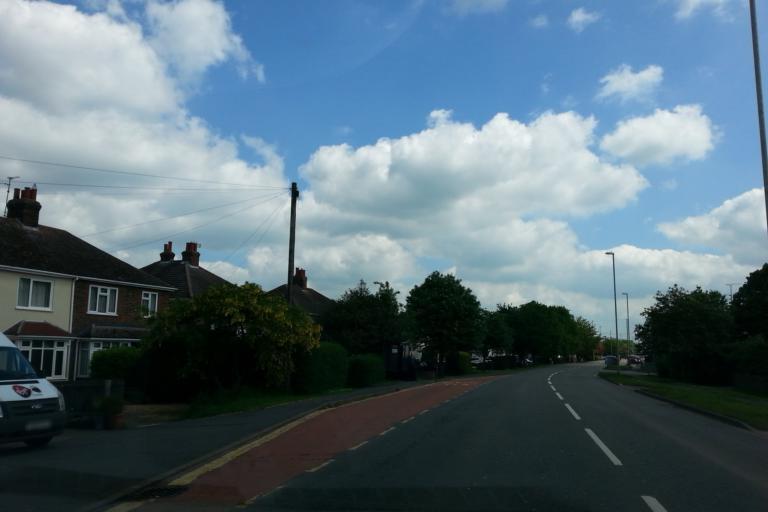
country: GB
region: England
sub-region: Cambridgeshire
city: Yaxley
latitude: 52.5177
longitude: -0.2591
